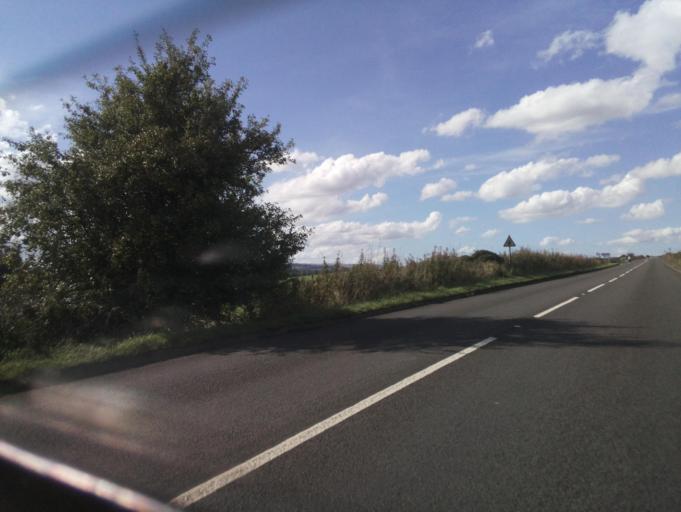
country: GB
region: Scotland
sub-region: Stirling
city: Plean
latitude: 56.0752
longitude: -3.8889
